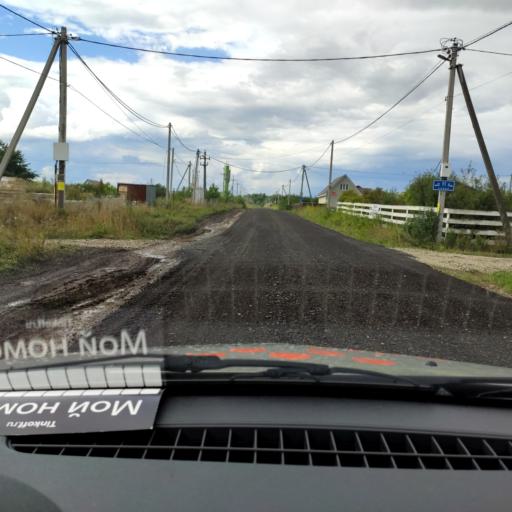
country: RU
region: Bashkortostan
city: Avdon
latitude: 54.5179
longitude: 55.8340
